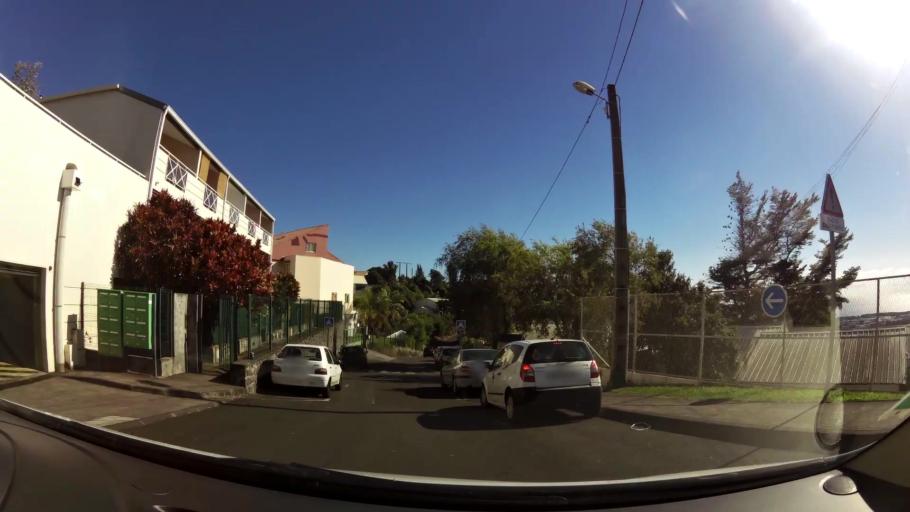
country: RE
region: Reunion
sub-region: Reunion
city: Saint-Denis
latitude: -20.9167
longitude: 55.4859
